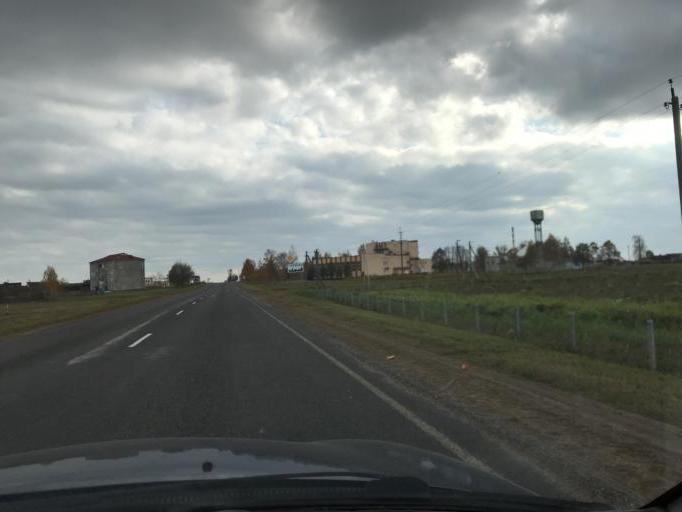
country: BY
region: Grodnenskaya
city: Lida
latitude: 53.7946
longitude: 25.1408
